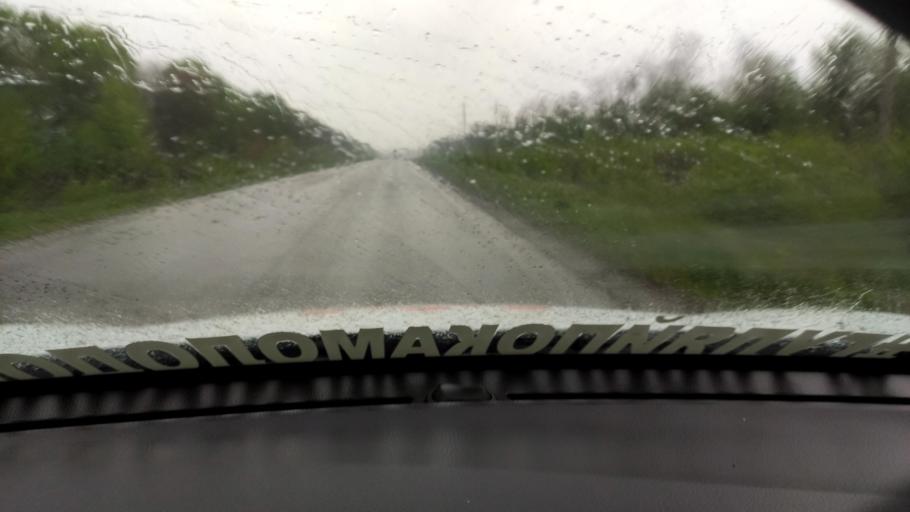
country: RU
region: Voronezj
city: Latnaya
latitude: 51.7583
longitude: 38.9180
